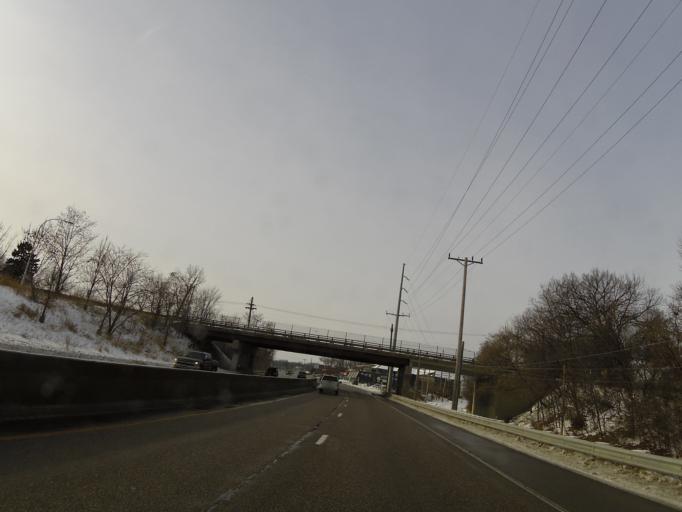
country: US
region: Minnesota
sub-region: Hennepin County
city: Excelsior
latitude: 44.9007
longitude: -93.5612
